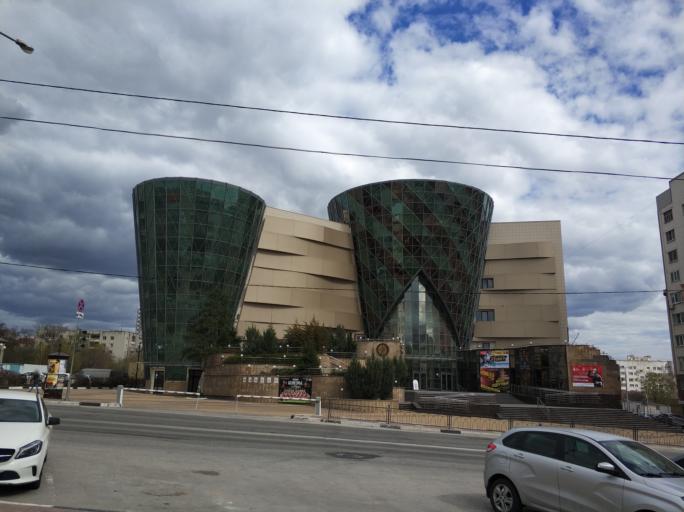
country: RU
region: Belgorod
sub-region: Belgorodskiy Rayon
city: Belgorod
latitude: 50.5990
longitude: 36.6023
